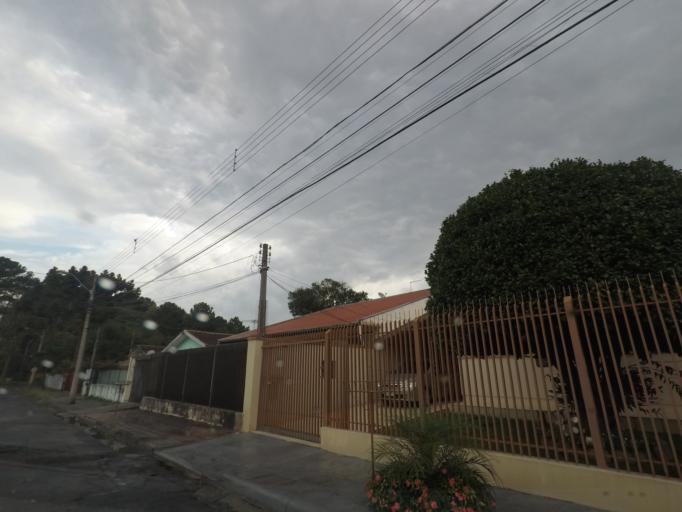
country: BR
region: Parana
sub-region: Sao Jose Dos Pinhais
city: Sao Jose dos Pinhais
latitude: -25.4966
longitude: -49.2447
